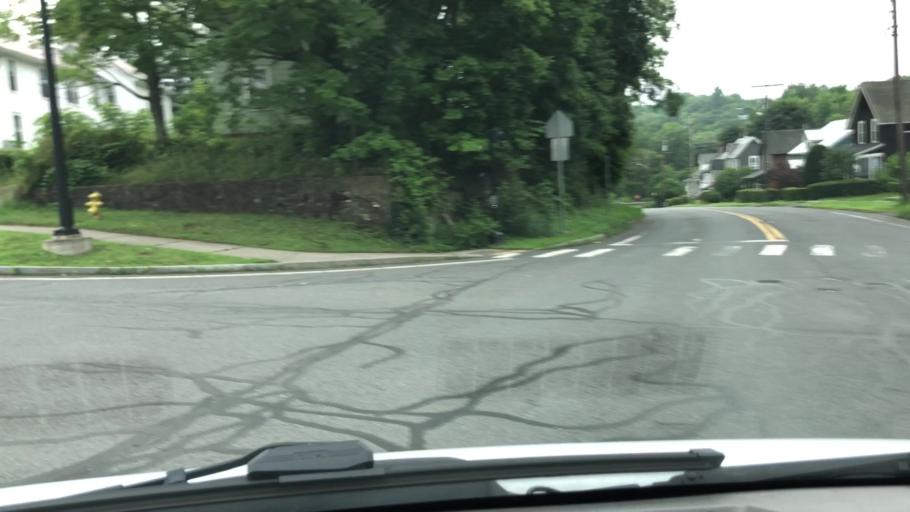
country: US
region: Massachusetts
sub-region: Franklin County
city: Greenfield
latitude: 42.5875
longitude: -72.6114
